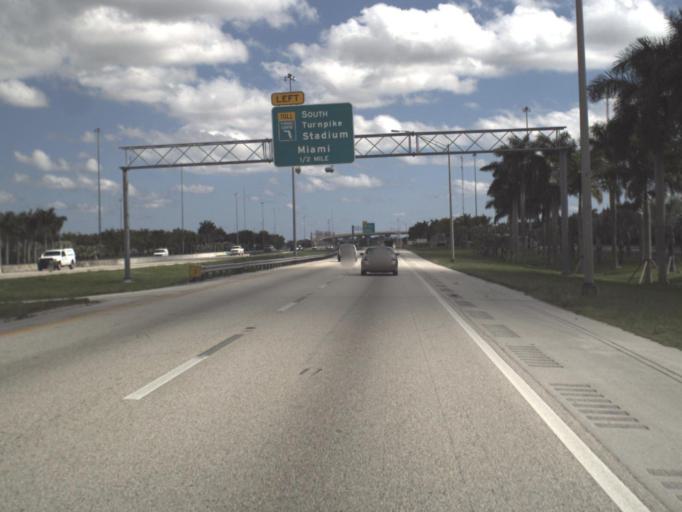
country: US
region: Florida
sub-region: Miami-Dade County
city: Lake Lucerne
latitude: 25.9724
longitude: -80.2419
